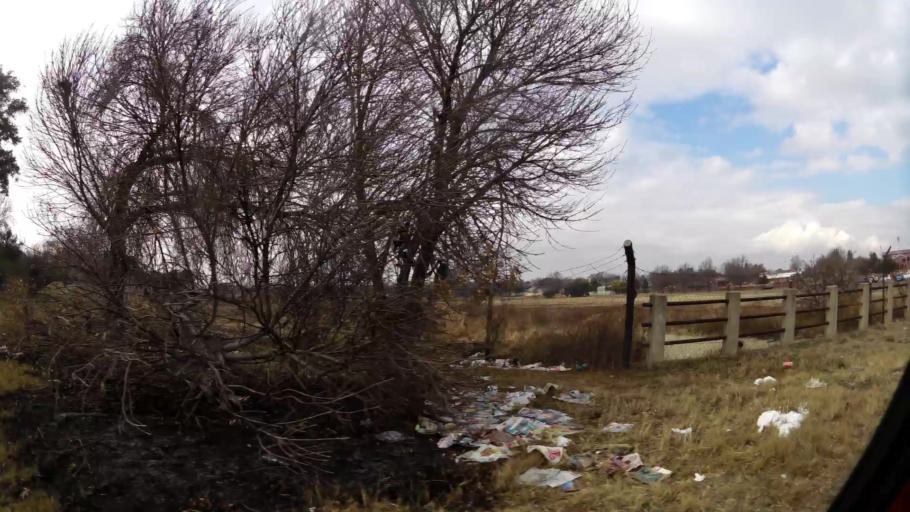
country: ZA
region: Gauteng
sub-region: Sedibeng District Municipality
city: Vanderbijlpark
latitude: -26.7134
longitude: 27.8533
